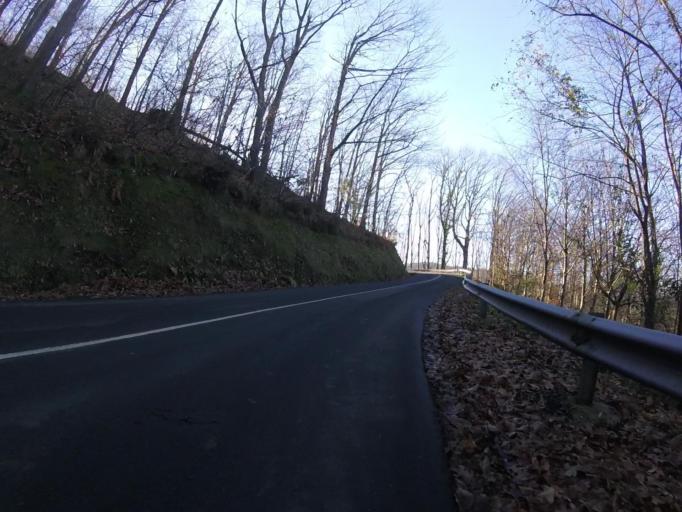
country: ES
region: Basque Country
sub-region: Provincia de Guipuzcoa
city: Irun
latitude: 43.3165
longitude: -1.7621
